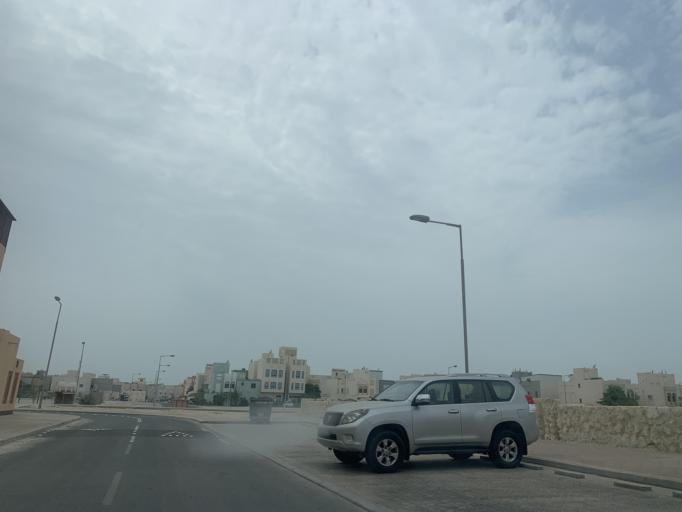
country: BH
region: Muharraq
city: Al Muharraq
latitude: 26.2833
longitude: 50.6408
